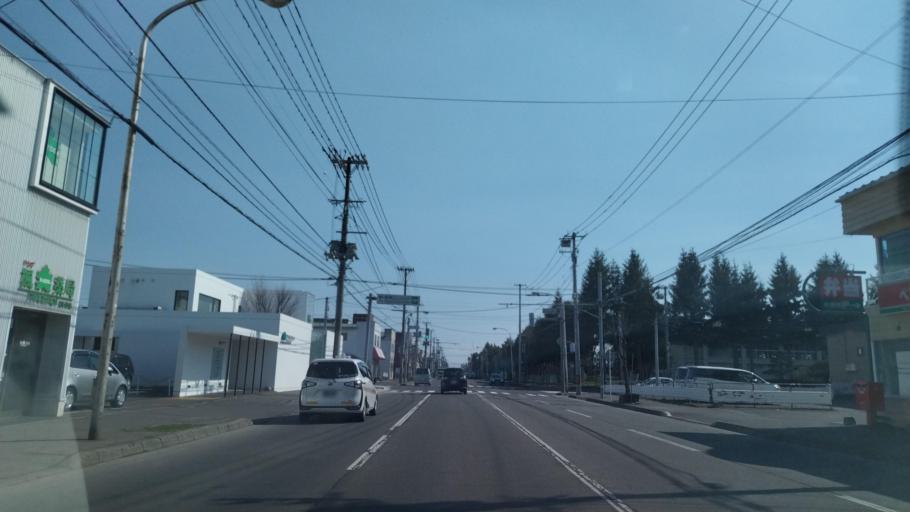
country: JP
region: Hokkaido
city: Obihiro
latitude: 42.9041
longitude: 143.1997
